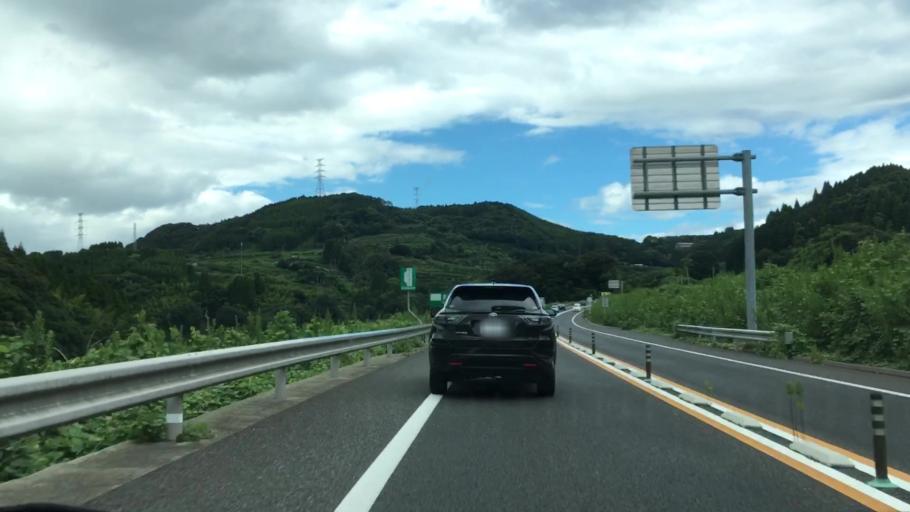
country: JP
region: Saga Prefecture
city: Karatsu
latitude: 33.3921
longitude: 129.9347
